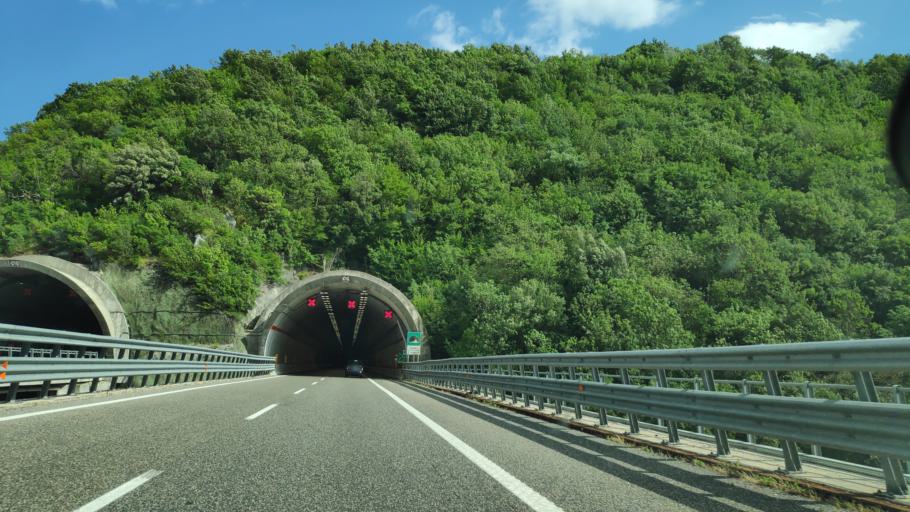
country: IT
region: Campania
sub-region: Provincia di Salerno
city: Sicignano degli Alburni
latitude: 40.6053
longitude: 15.3003
